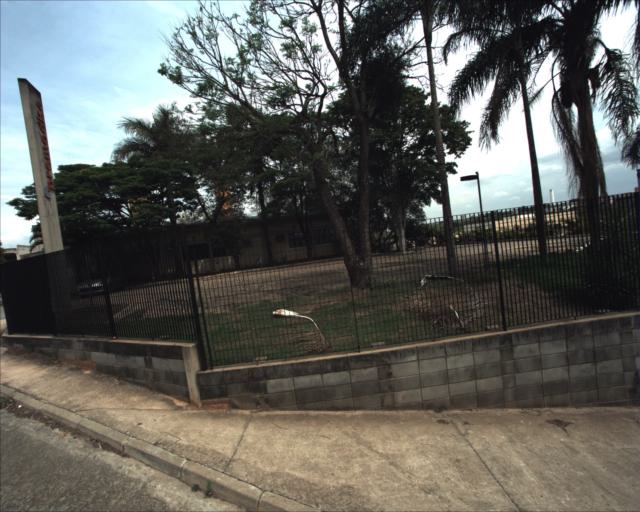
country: BR
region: Sao Paulo
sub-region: Sorocaba
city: Sorocaba
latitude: -23.4280
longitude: -47.4320
